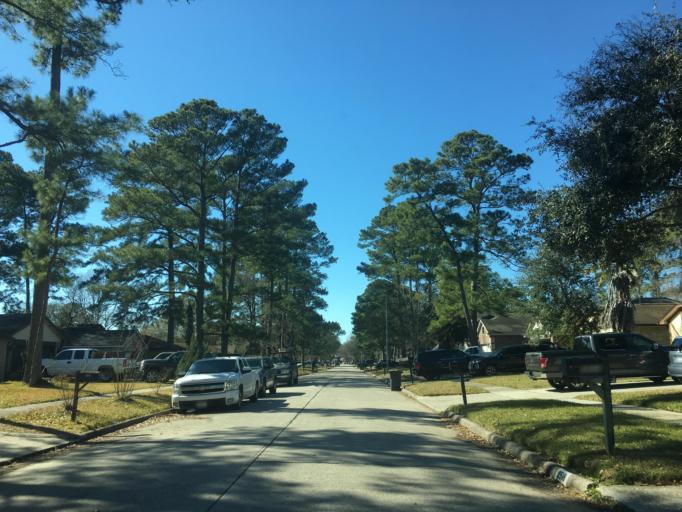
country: US
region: Texas
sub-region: Harris County
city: Spring
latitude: 30.0894
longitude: -95.4686
